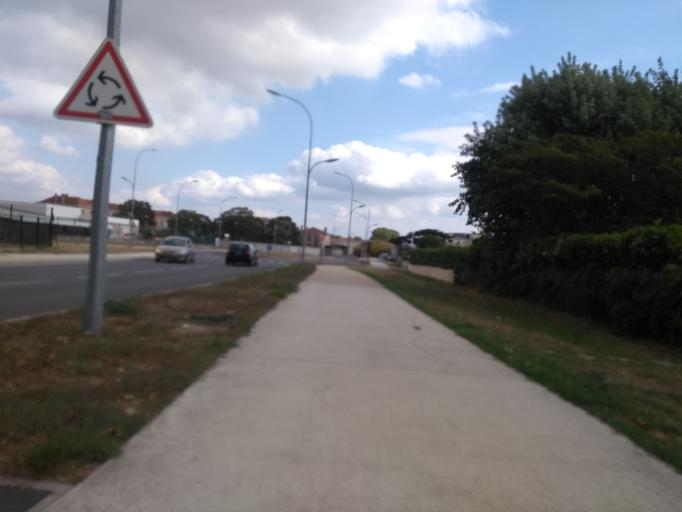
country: FR
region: Aquitaine
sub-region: Departement de la Gironde
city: Talence
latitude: 44.7962
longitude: -0.5770
